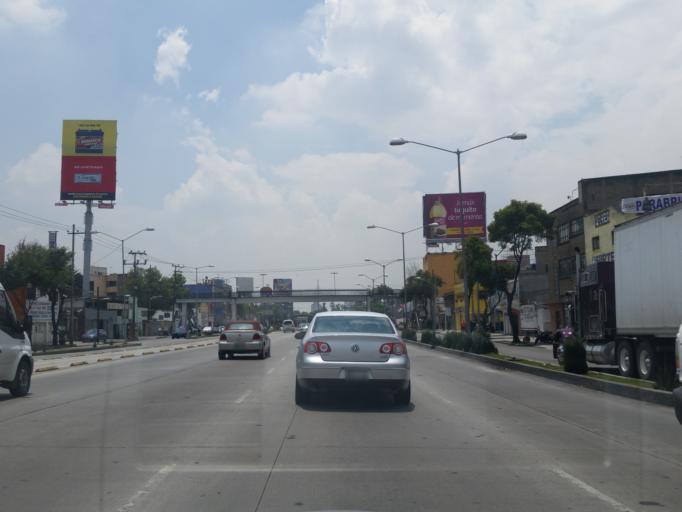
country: MX
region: Mexico City
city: Cuauhtemoc
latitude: 19.4704
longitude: -99.1449
